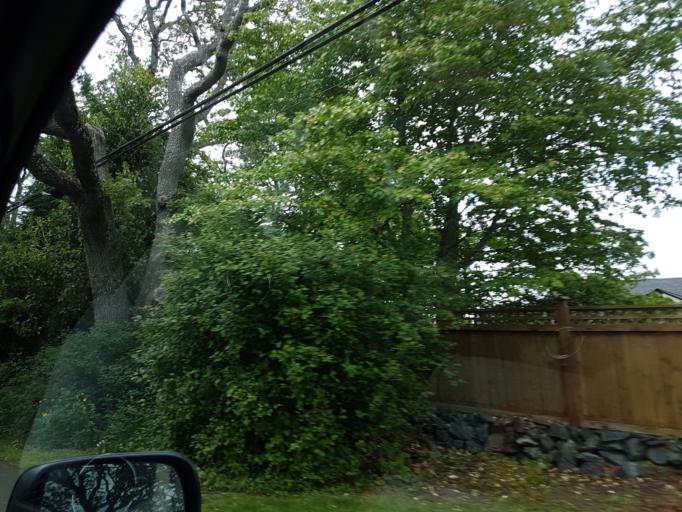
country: CA
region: British Columbia
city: Oak Bay
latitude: 48.4818
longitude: -123.3394
